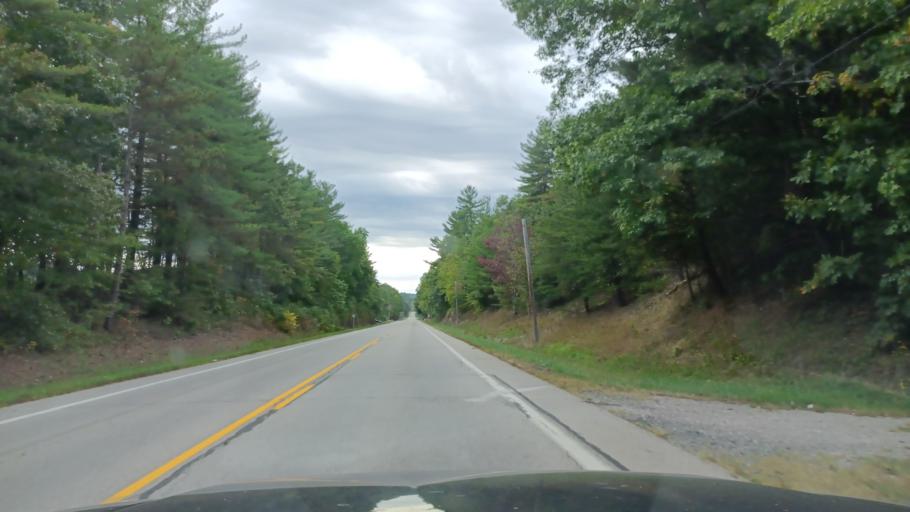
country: US
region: Ohio
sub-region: Vinton County
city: McArthur
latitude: 39.2385
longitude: -82.4002
